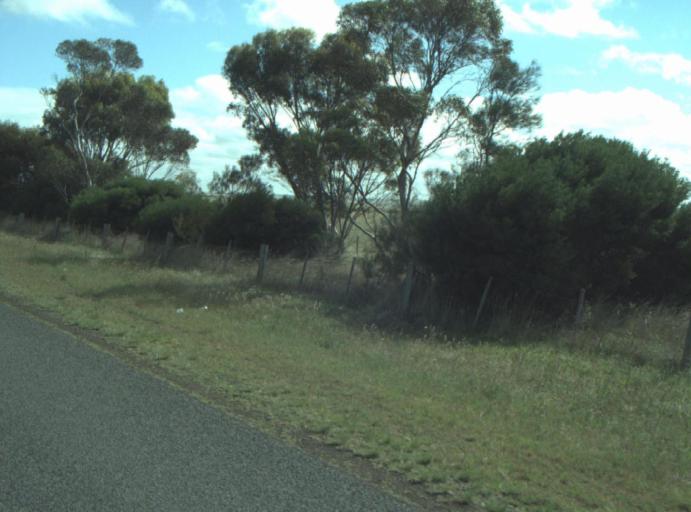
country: AU
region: Victoria
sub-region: Greater Geelong
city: Lara
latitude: -37.9495
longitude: 144.3081
